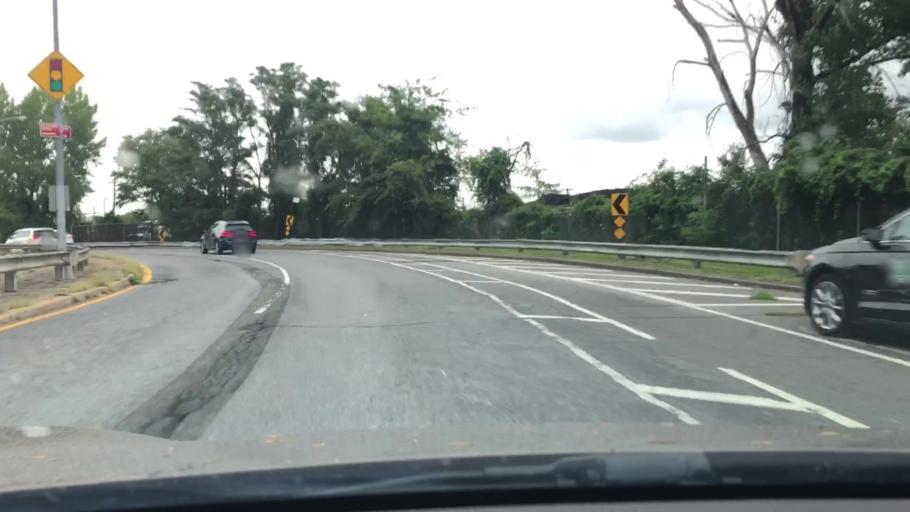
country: US
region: New York
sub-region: Bronx
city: Eastchester
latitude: 40.8793
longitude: -73.8225
